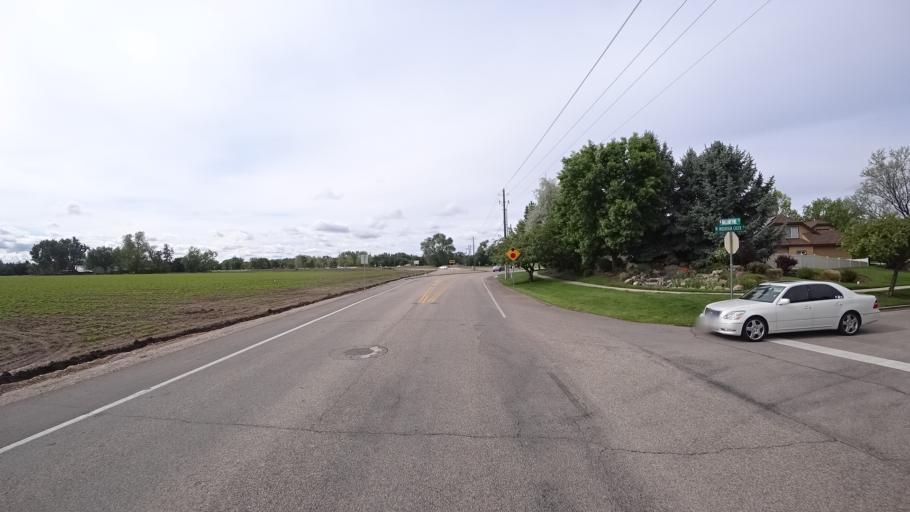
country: US
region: Idaho
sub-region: Ada County
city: Eagle
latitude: 43.6981
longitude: -116.3791
